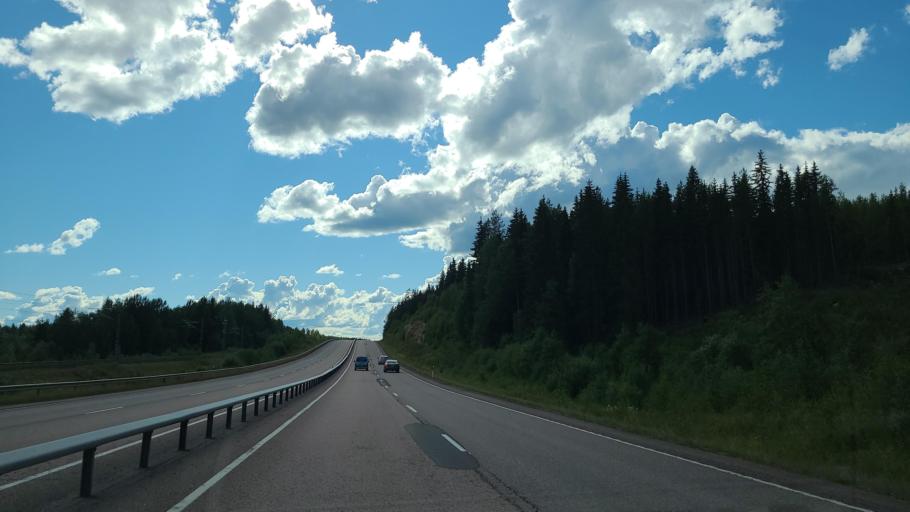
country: FI
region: Pirkanmaa
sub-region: Tampere
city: Kuhmalahti
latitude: 61.7341
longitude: 24.7319
